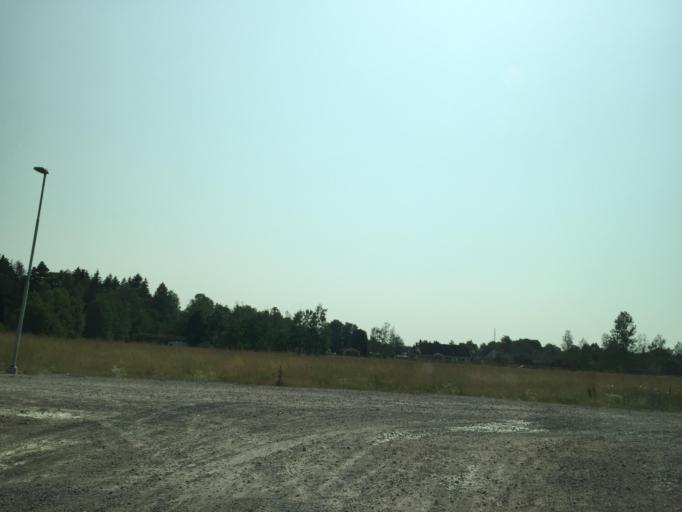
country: SE
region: Vaestra Goetaland
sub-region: Vanersborgs Kommun
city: Vanersborg
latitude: 58.3606
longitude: 12.2823
